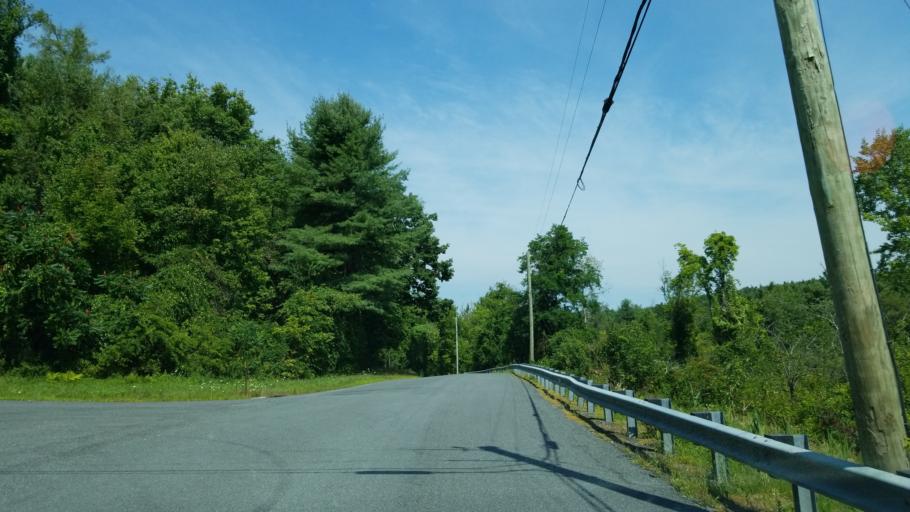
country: US
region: Connecticut
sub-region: Litchfield County
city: Winchester Center
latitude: 41.8782
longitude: -73.2064
